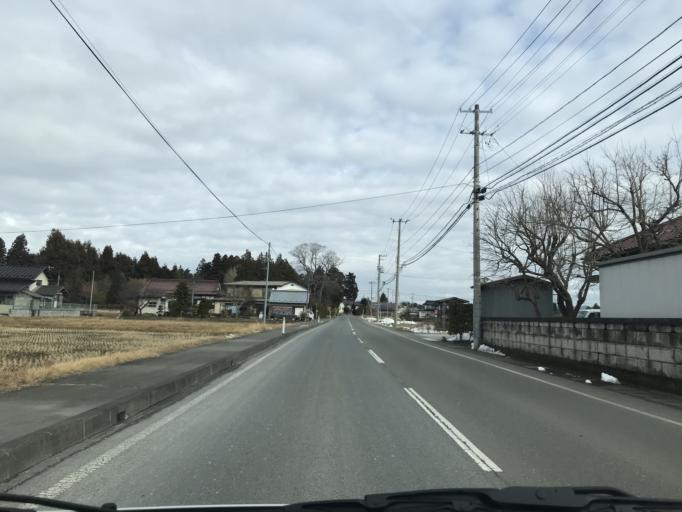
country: JP
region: Iwate
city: Mizusawa
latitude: 39.0672
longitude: 141.1598
